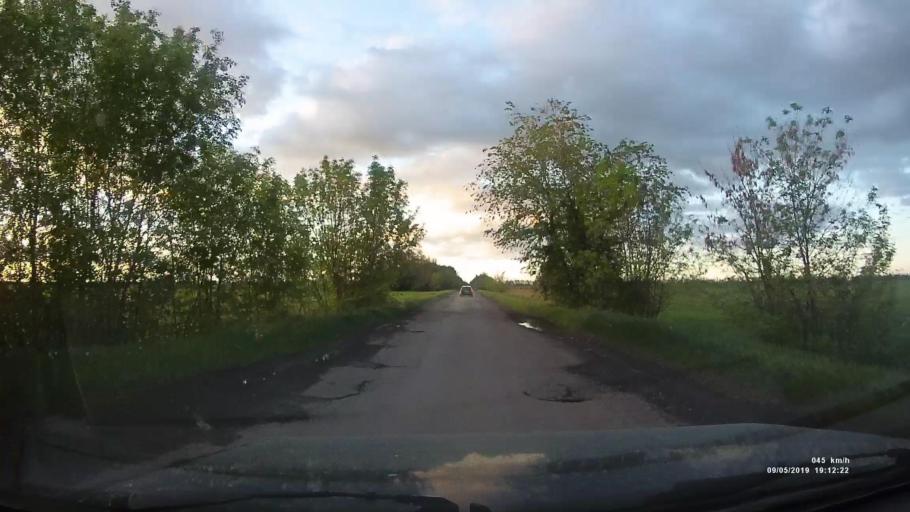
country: RU
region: Krasnodarskiy
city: Kanelovskaya
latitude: 46.7412
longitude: 39.2137
